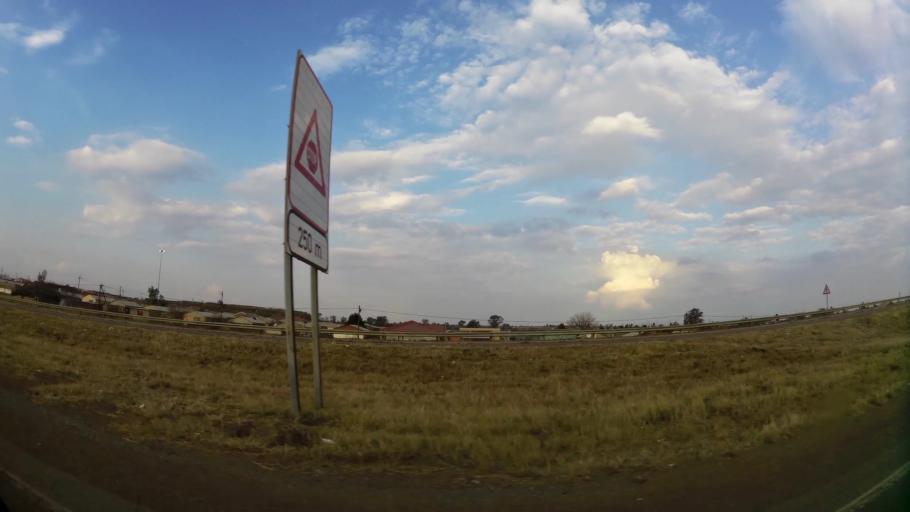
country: ZA
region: Gauteng
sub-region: Sedibeng District Municipality
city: Vanderbijlpark
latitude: -26.6041
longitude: 27.8174
